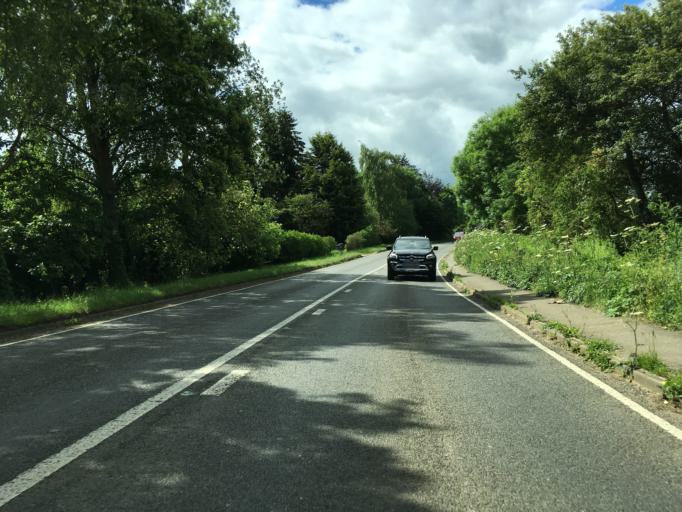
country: GB
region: England
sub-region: Oxfordshire
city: Bloxham
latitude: 52.0329
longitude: -1.3653
